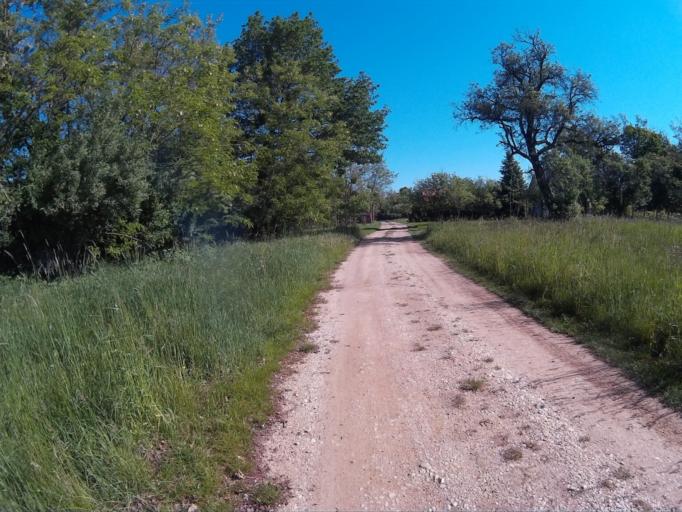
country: HU
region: Vas
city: Kormend
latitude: 46.9886
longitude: 16.6668
